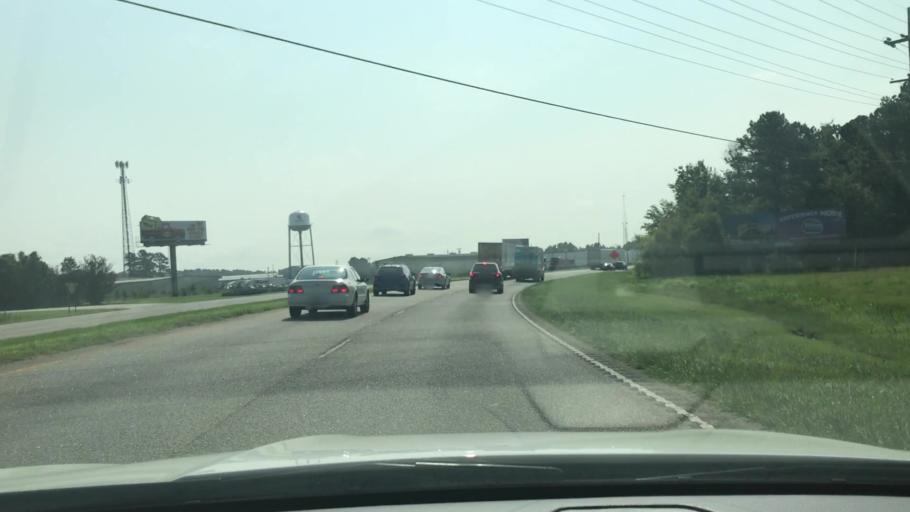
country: US
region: South Carolina
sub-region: Horry County
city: Red Hill
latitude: 33.8065
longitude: -79.0131
